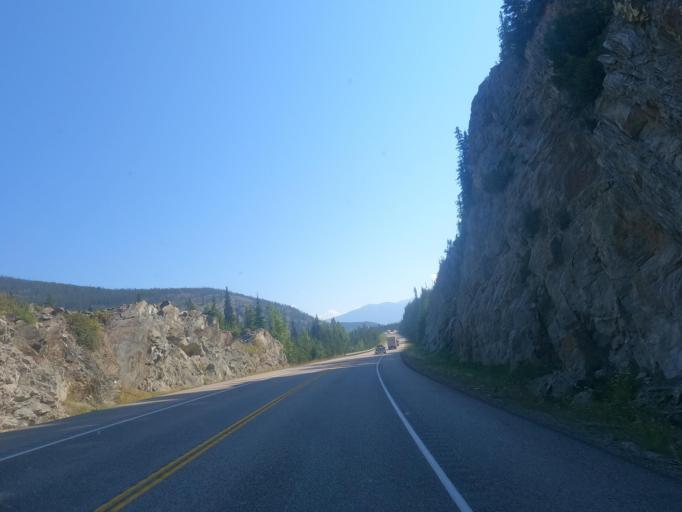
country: CA
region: Alberta
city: Jasper Park Lodge
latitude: 52.8627
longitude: -118.2151
